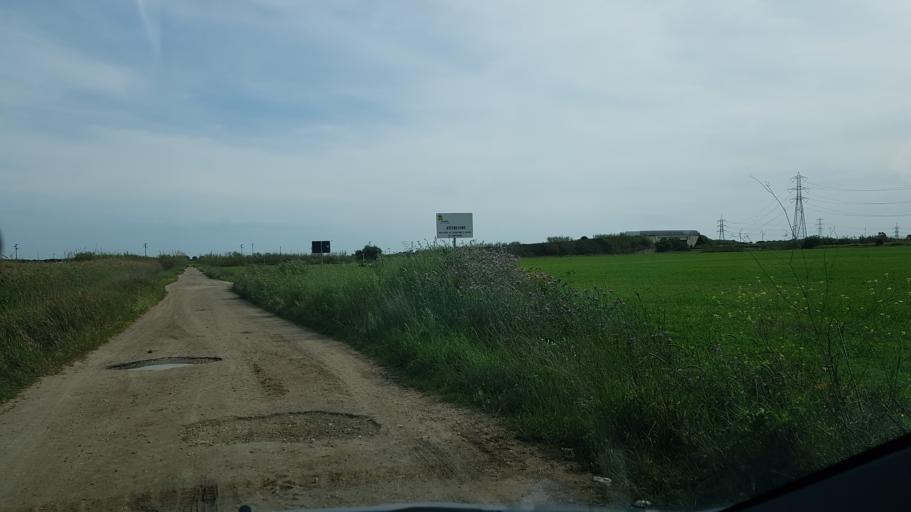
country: IT
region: Apulia
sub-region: Provincia di Brindisi
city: La Rosa
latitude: 40.6026
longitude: 17.9698
